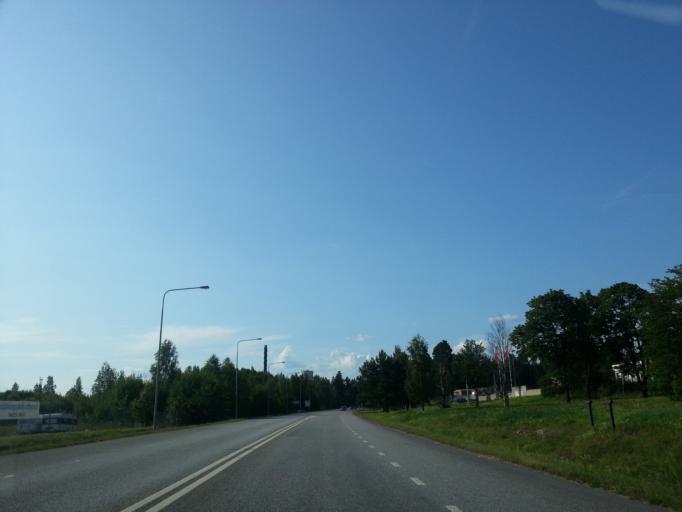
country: SE
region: Vaestmanland
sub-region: Fagersta Kommun
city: Fagersta
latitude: 60.0064
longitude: 15.7861
